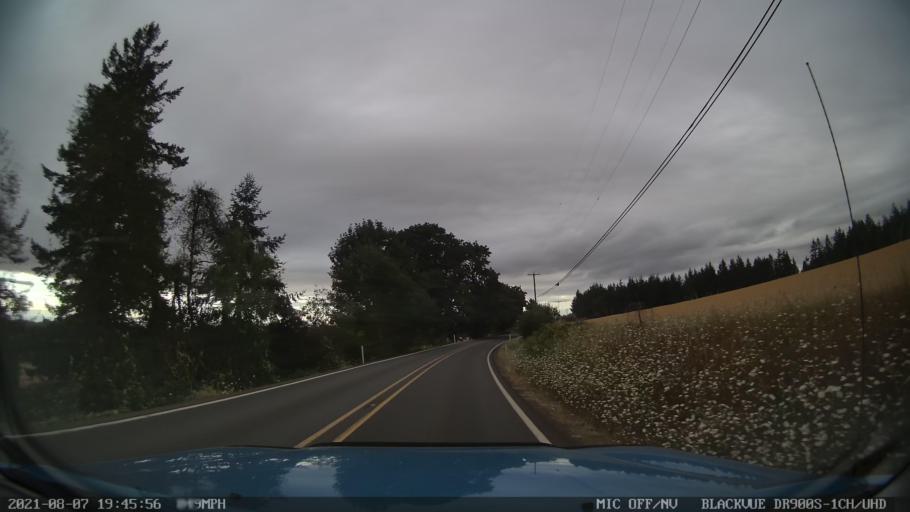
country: US
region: Oregon
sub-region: Marion County
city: Silverton
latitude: 44.9531
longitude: -122.7002
